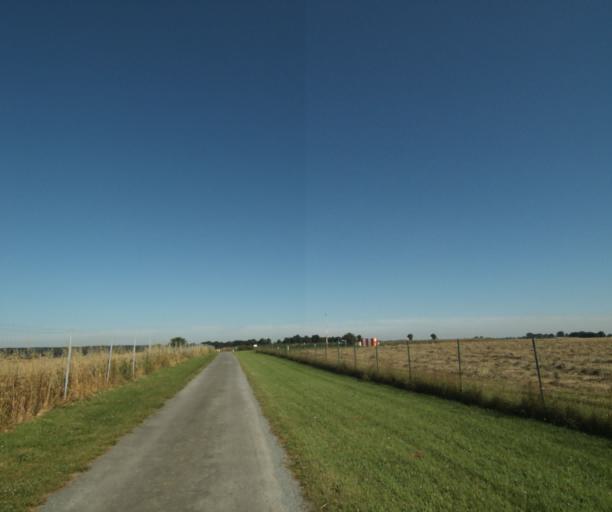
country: FR
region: Pays de la Loire
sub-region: Departement de la Mayenne
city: Laval
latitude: 48.0301
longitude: -0.7457
